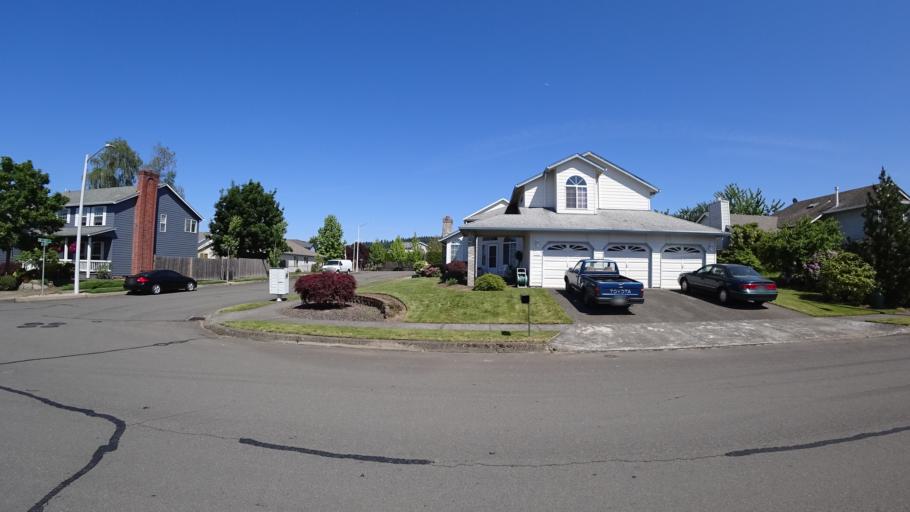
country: US
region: Oregon
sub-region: Multnomah County
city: Gresham
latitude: 45.4730
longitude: -122.4640
